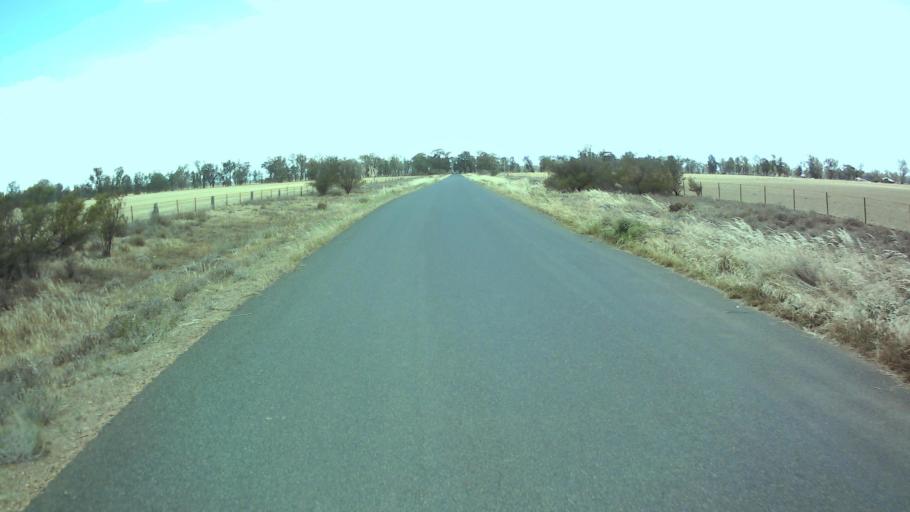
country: AU
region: New South Wales
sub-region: Weddin
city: Grenfell
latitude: -34.0701
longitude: 147.7777
